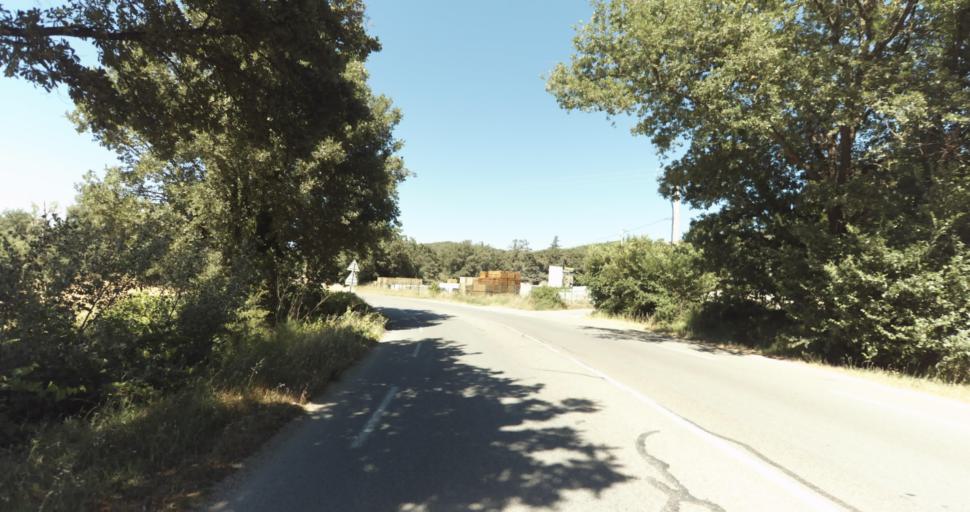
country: FR
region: Provence-Alpes-Cote d'Azur
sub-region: Departement du Var
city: Gassin
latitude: 43.2279
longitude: 6.5734
